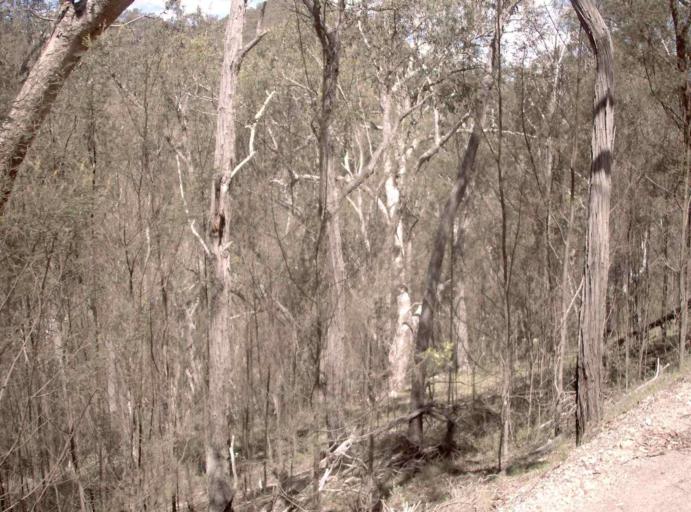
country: AU
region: New South Wales
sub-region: Bombala
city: Bombala
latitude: -37.1062
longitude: 148.6410
